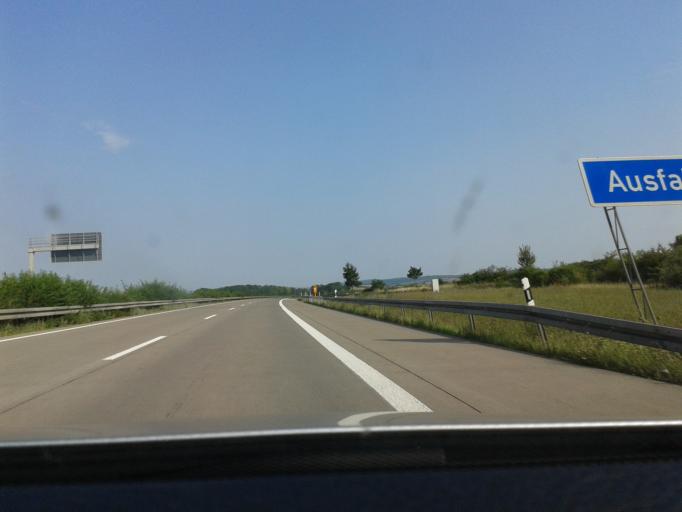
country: DE
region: Thuringia
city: Nordhausen
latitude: 51.4873
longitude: 10.7495
